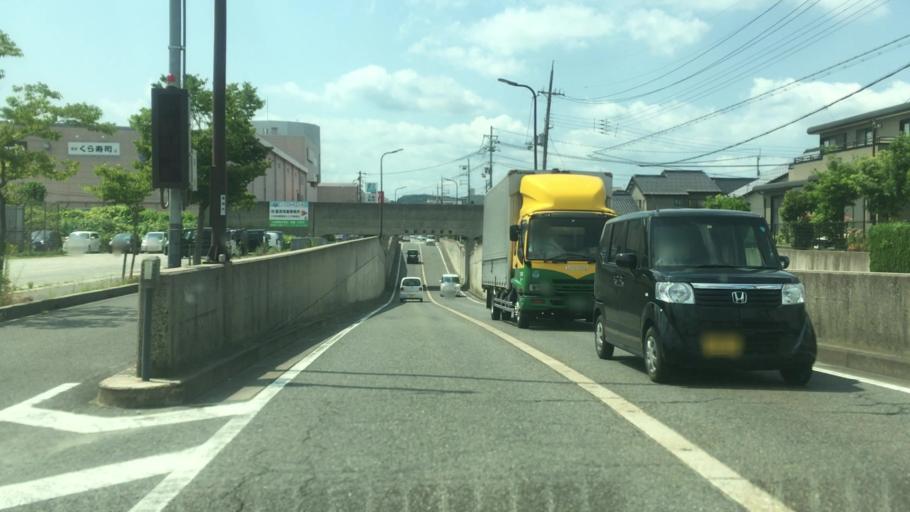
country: JP
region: Hyogo
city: Toyooka
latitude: 35.5521
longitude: 134.8155
